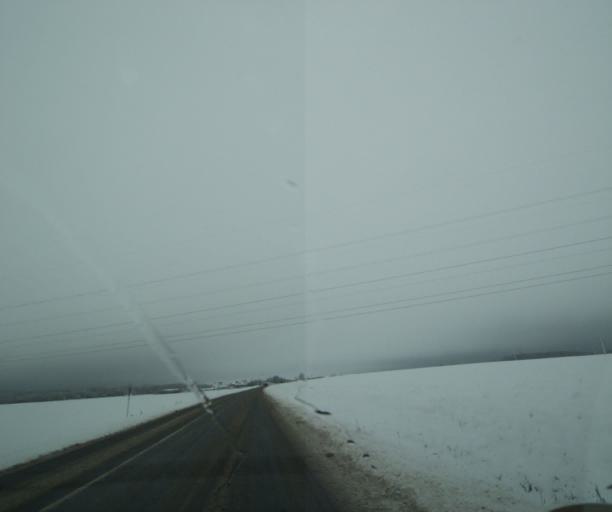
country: FR
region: Champagne-Ardenne
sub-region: Departement de la Haute-Marne
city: Wassy
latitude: 48.5171
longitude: 4.9338
